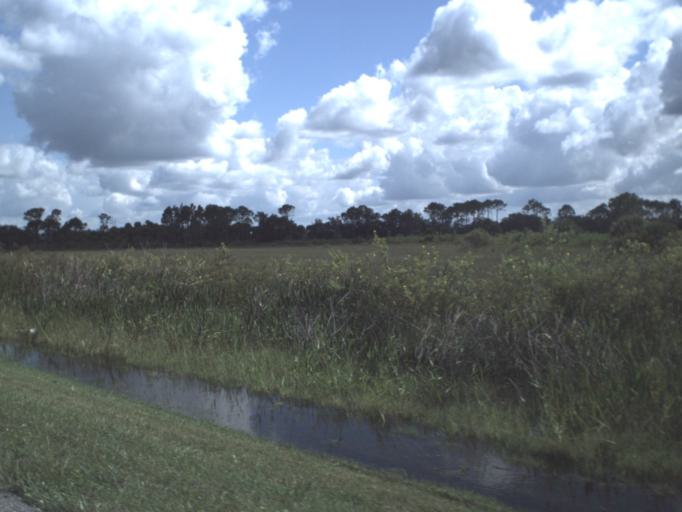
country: US
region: Florida
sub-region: Sarasota County
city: Warm Mineral Springs
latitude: 27.2106
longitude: -82.2575
